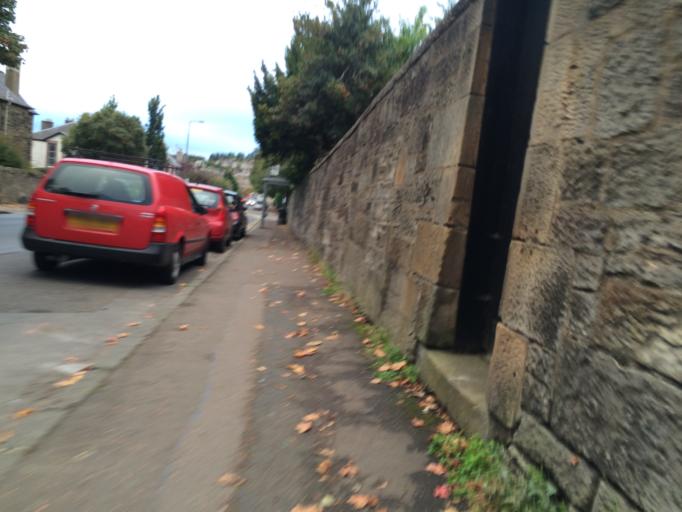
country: GB
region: Scotland
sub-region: Edinburgh
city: Edinburgh
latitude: 55.9295
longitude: -3.1890
